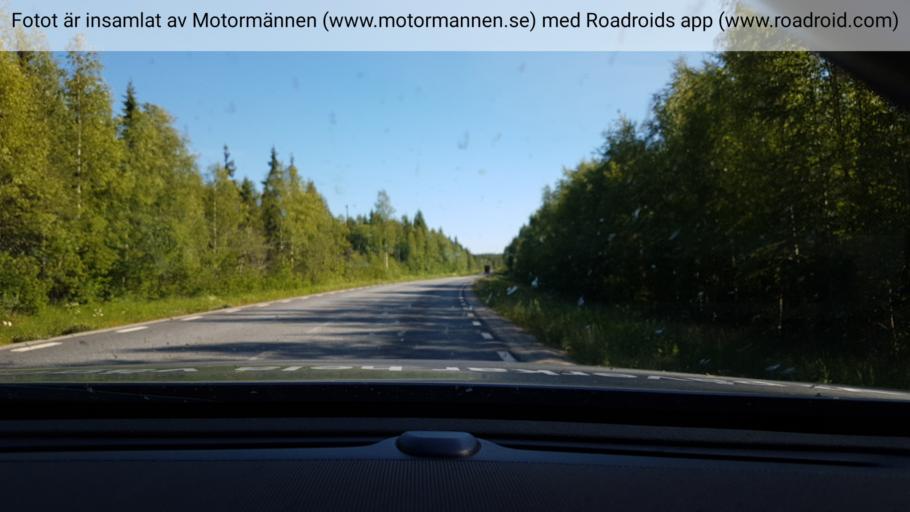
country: SE
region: Vaesterbotten
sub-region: Bjurholms Kommun
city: Bjurholm
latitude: 64.3749
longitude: 19.1399
